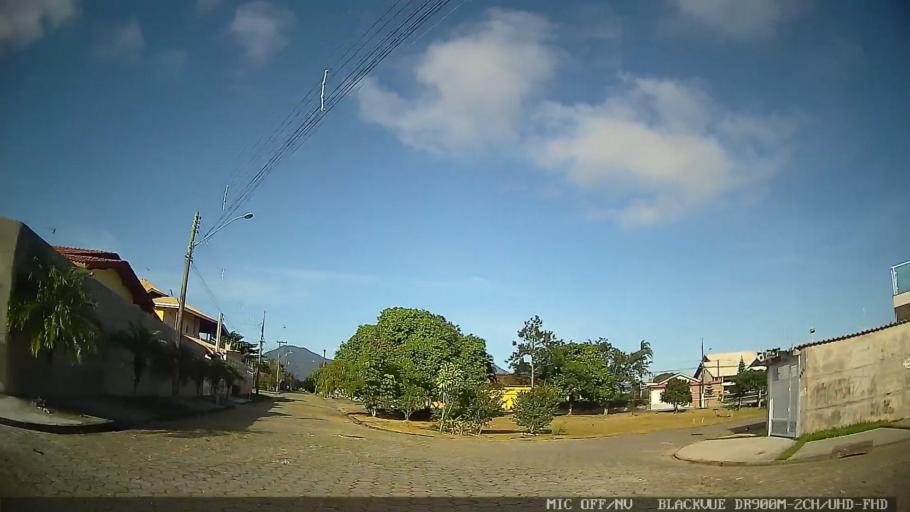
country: BR
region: Sao Paulo
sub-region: Peruibe
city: Peruibe
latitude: -24.2980
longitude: -46.9775
